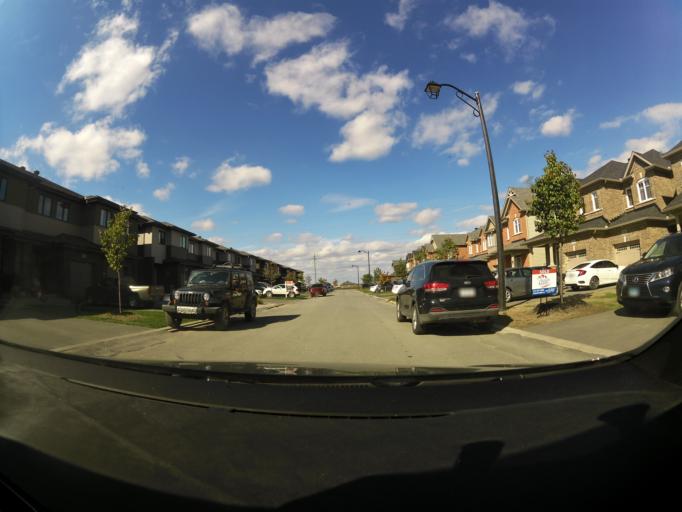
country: CA
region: Ontario
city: Bells Corners
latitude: 45.2790
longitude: -75.8827
